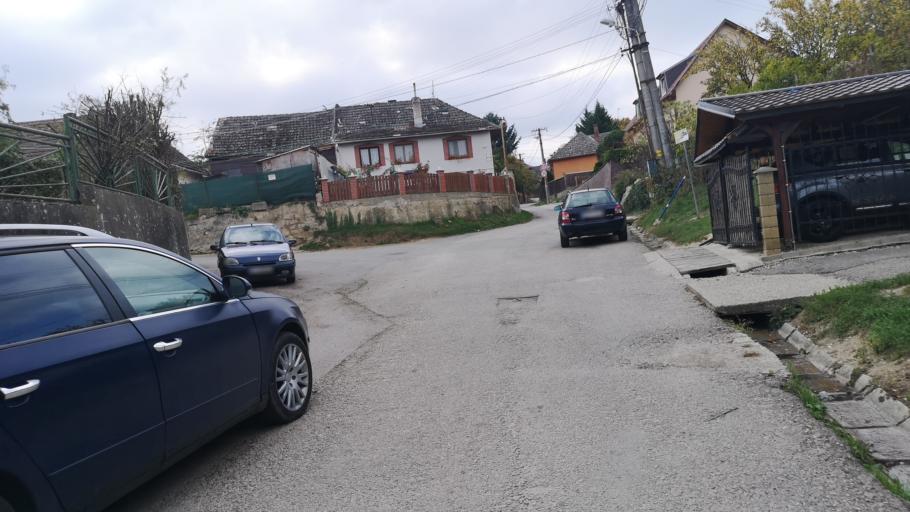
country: SK
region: Nitriansky
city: Cachtice
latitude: 48.7149
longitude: 17.7825
